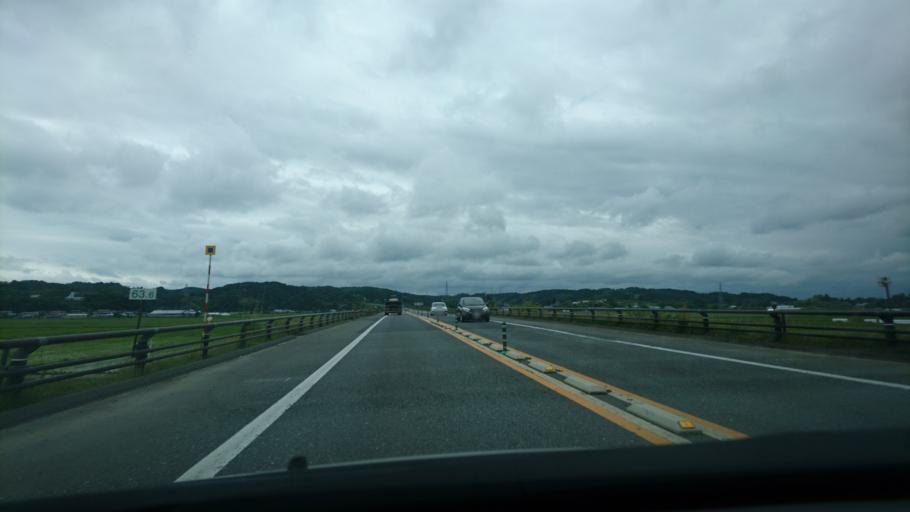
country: JP
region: Miyagi
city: Wakuya
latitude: 38.6585
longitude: 141.2649
